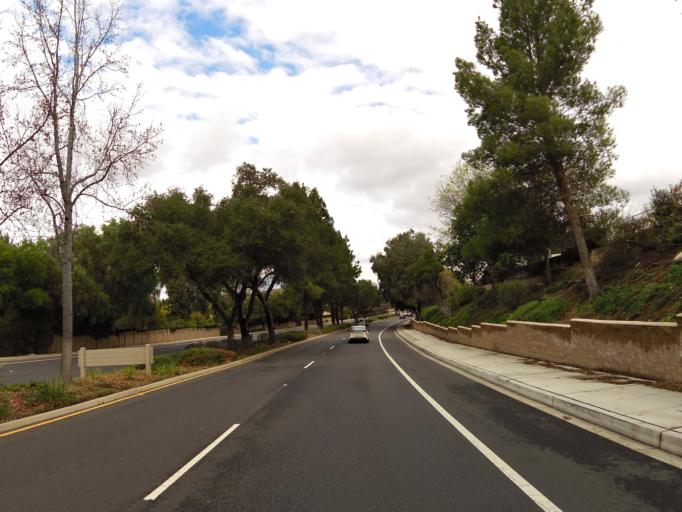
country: US
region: California
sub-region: Ventura County
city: Thousand Oaks
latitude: 34.1919
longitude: -118.8741
